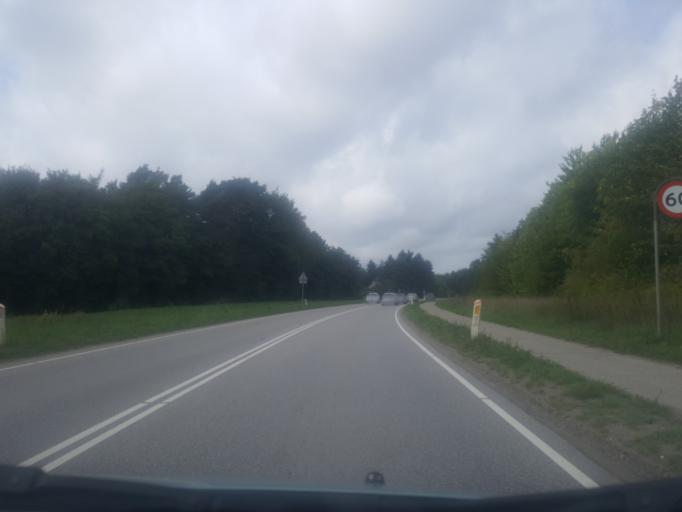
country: DK
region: Zealand
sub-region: Soro Kommune
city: Soro
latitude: 55.4667
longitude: 11.5499
